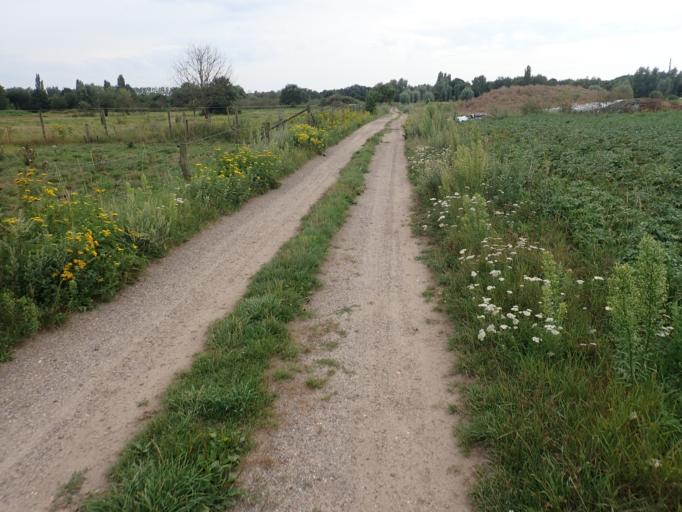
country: BE
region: Flanders
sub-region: Provincie Antwerpen
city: Ranst
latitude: 51.2131
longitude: 4.5595
